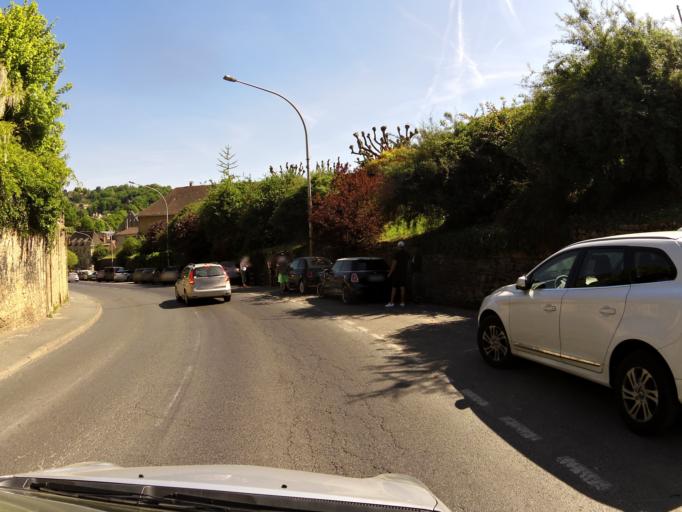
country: FR
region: Aquitaine
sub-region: Departement de la Dordogne
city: Sarlat-la-Caneda
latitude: 44.8885
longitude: 1.2143
